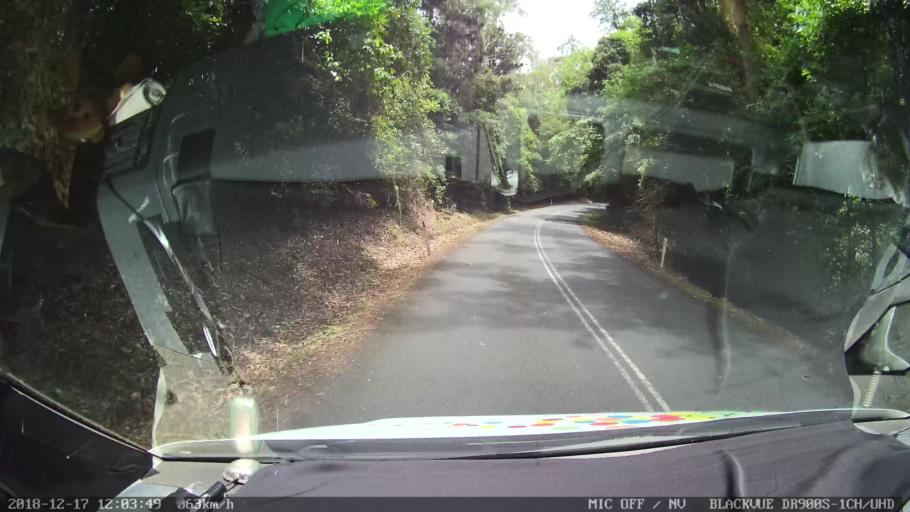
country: AU
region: New South Wales
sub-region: Kyogle
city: Kyogle
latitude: -28.5047
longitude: 152.5683
